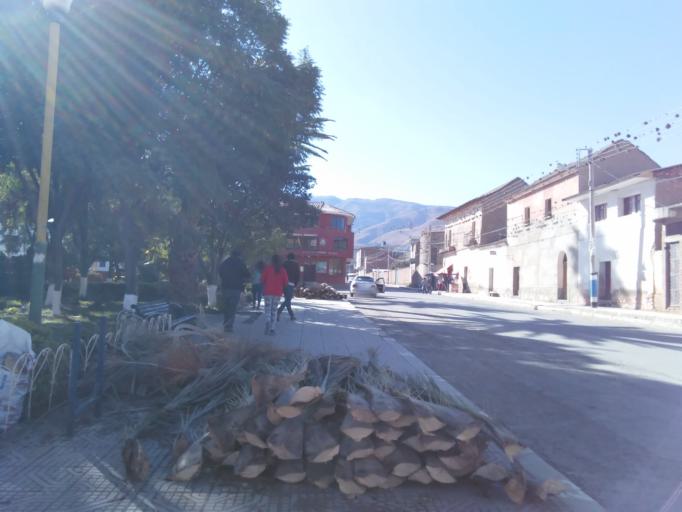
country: BO
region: Cochabamba
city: Punata
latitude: -17.5232
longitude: -65.8940
